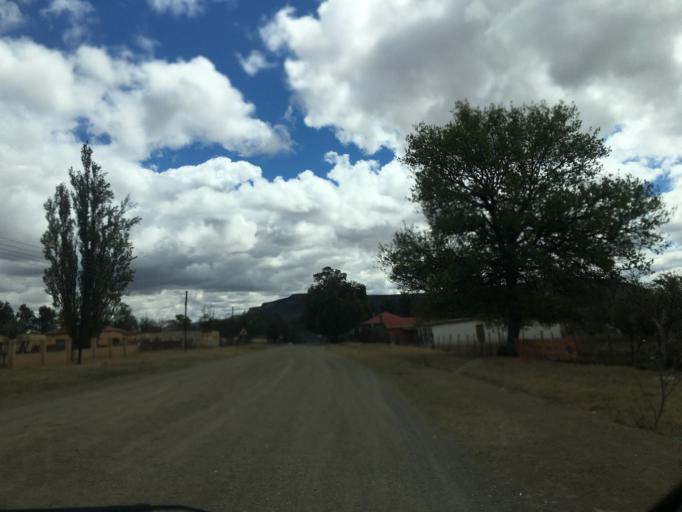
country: ZA
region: Eastern Cape
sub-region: Chris Hani District Municipality
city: Cala
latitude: -31.5221
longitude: 27.6999
